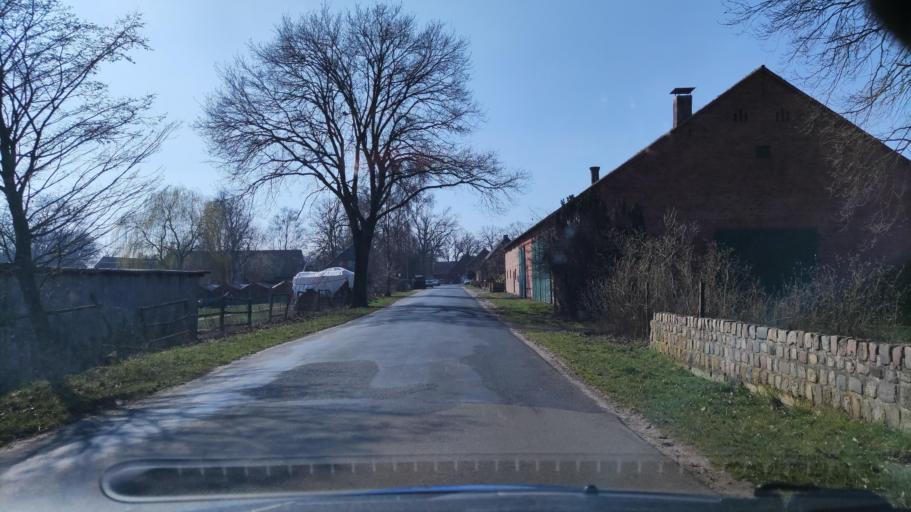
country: DE
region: Lower Saxony
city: Kusten
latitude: 52.9918
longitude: 11.0648
